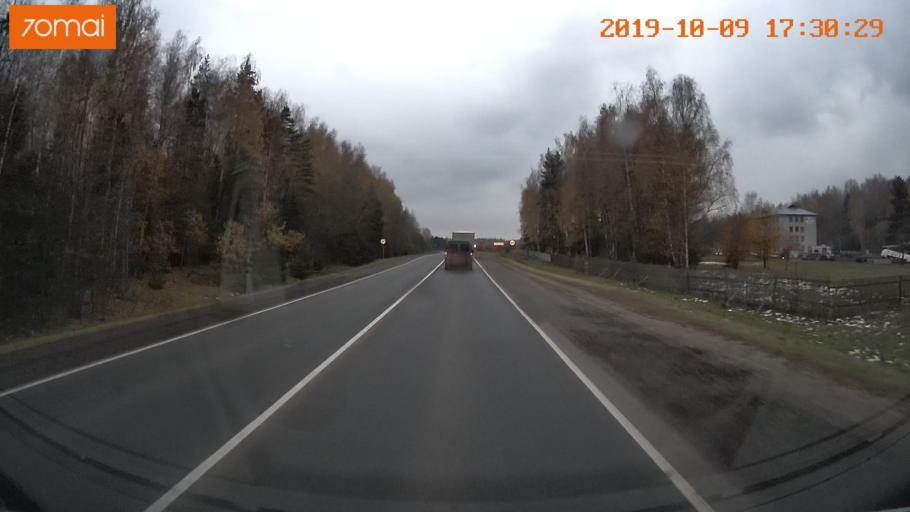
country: RU
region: Ivanovo
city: Bogorodskoye
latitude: 57.1424
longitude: 41.0488
